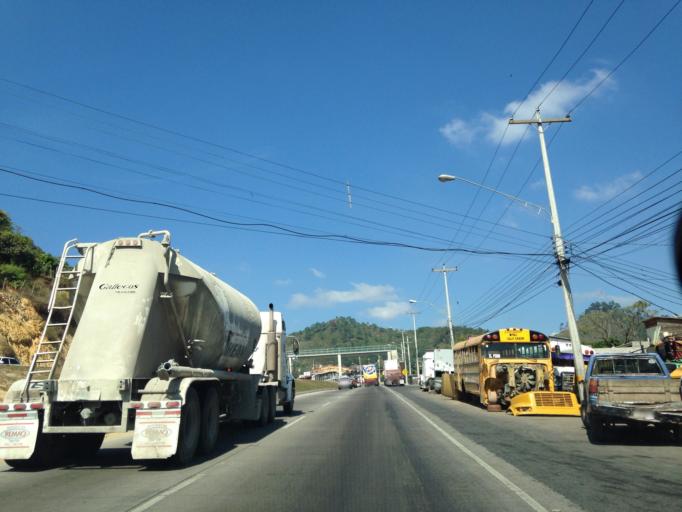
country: HN
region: Francisco Morazan
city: El Lolo
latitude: 14.1209
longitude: -87.2597
